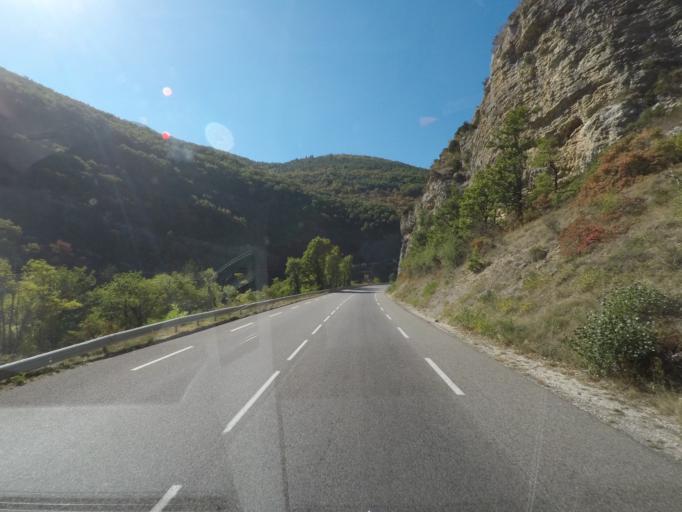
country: FR
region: Rhone-Alpes
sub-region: Departement de la Drome
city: Aouste-sur-Sye
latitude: 44.6907
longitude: 5.2132
